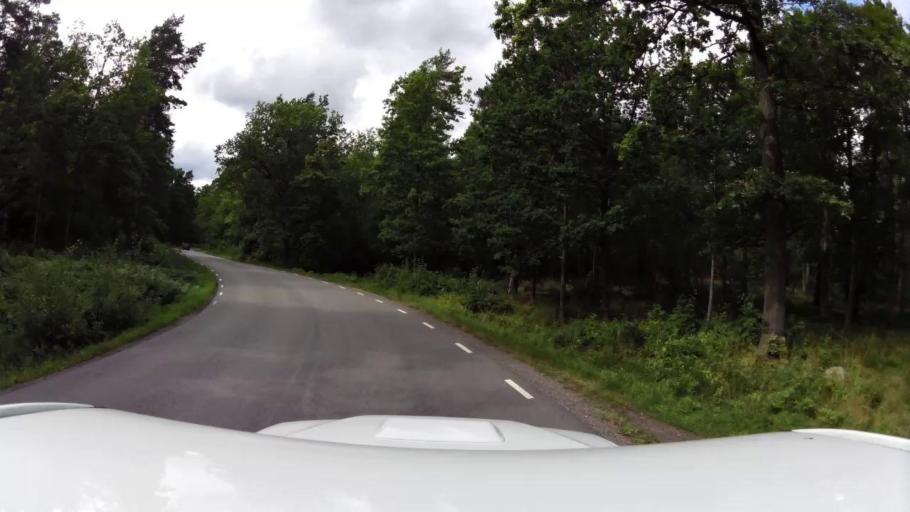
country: SE
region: OEstergoetland
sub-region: Linkopings Kommun
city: Linkoping
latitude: 58.3703
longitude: 15.5765
